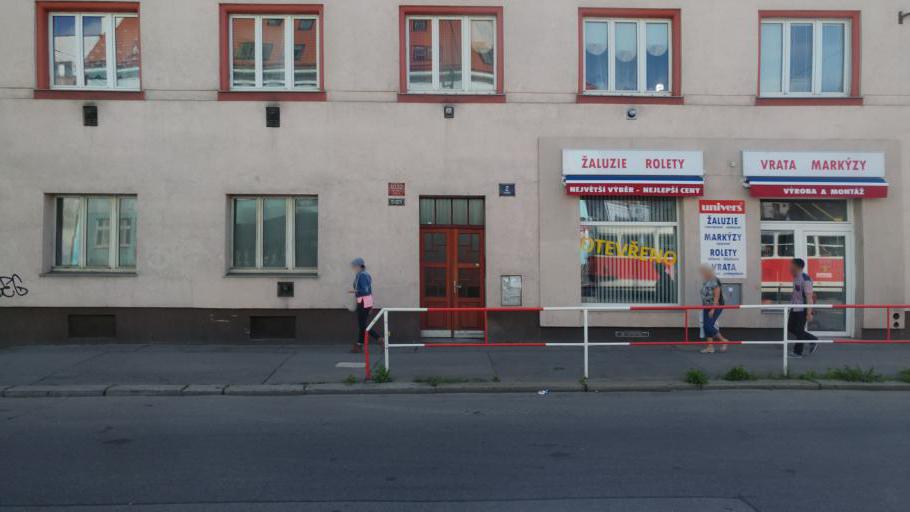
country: CZ
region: Praha
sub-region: Praha 8
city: Liben
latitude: 50.0715
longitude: 14.4873
